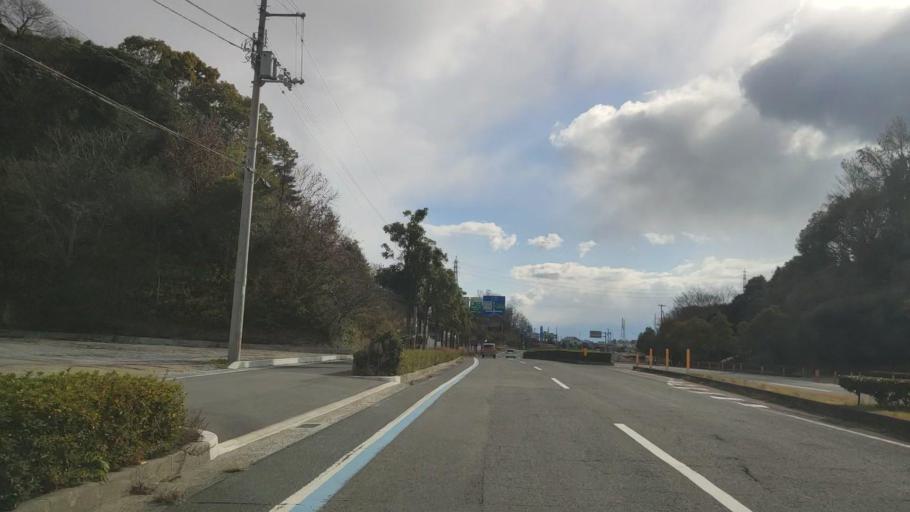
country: JP
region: Ehime
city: Hojo
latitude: 34.0573
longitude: 132.9733
